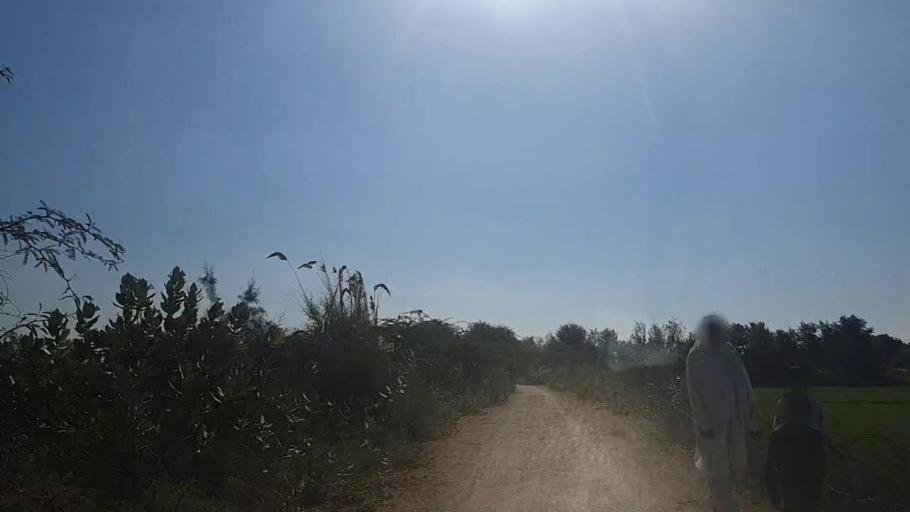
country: PK
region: Sindh
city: Khadro
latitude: 26.1523
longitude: 68.8378
